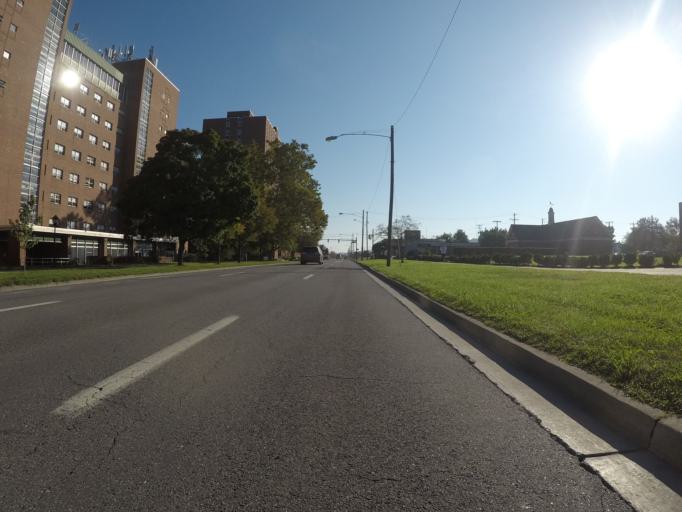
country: US
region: West Virginia
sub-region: Cabell County
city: Huntington
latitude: 38.4221
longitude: -82.4271
